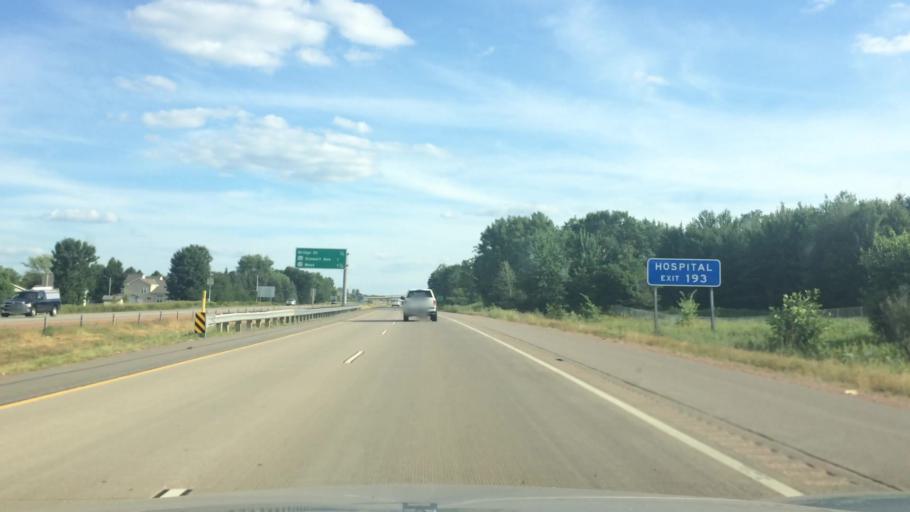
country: US
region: Wisconsin
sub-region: Marathon County
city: Wausau
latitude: 44.9791
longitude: -89.6575
